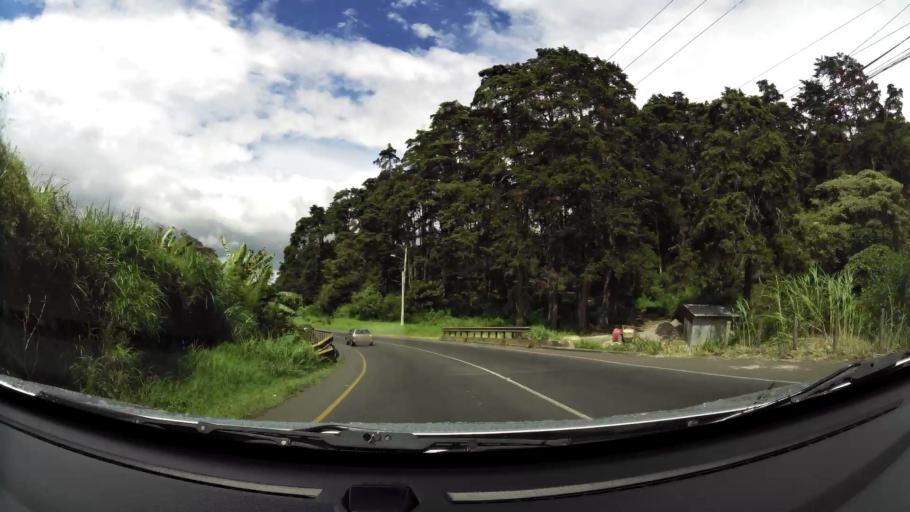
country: CR
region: Cartago
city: Tres Rios
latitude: 9.9063
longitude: -83.9585
